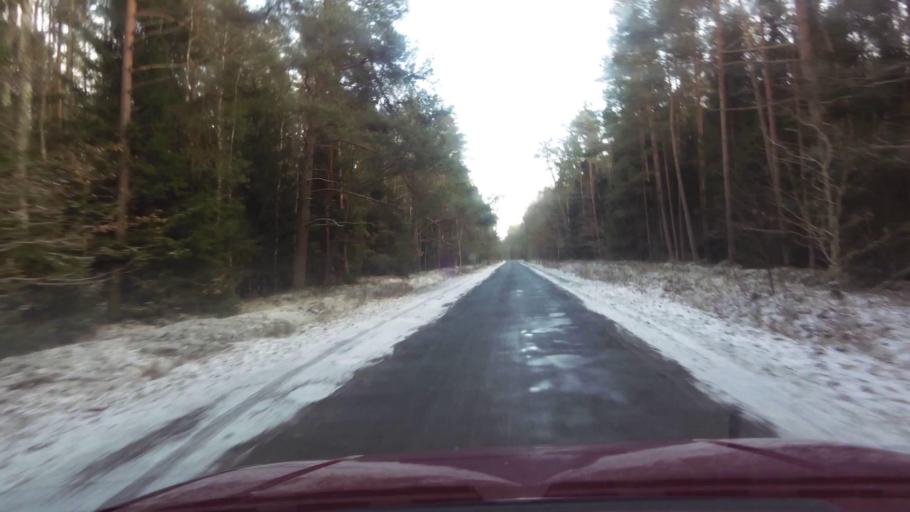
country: PL
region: West Pomeranian Voivodeship
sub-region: Powiat bialogardzki
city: Bialogard
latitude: 54.1042
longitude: 16.0301
